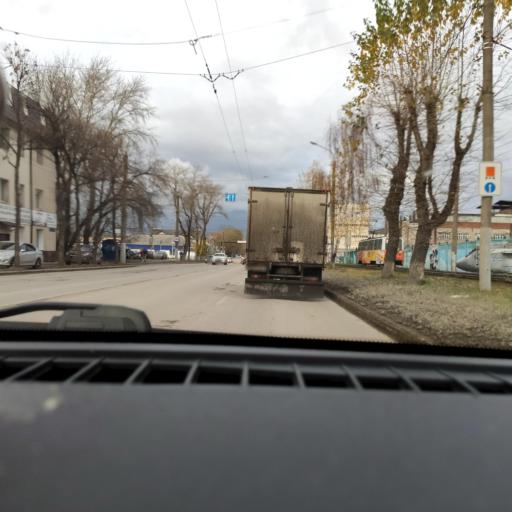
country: RU
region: Perm
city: Perm
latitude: 57.9741
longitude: 56.2465
